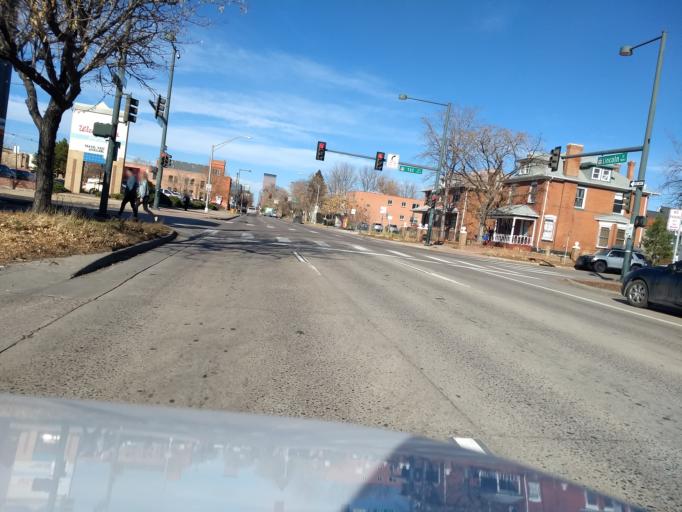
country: US
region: Colorado
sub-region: Denver County
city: Denver
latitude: 39.7181
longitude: -104.9863
